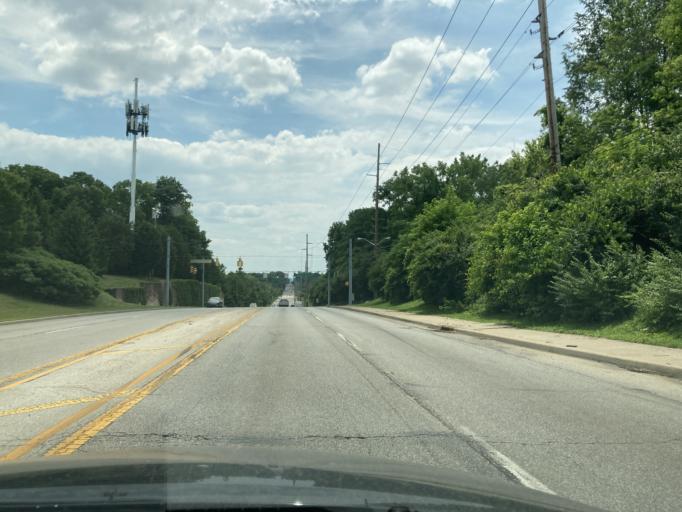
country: US
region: Indiana
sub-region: Marion County
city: Broad Ripple
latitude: 39.8400
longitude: -86.1882
